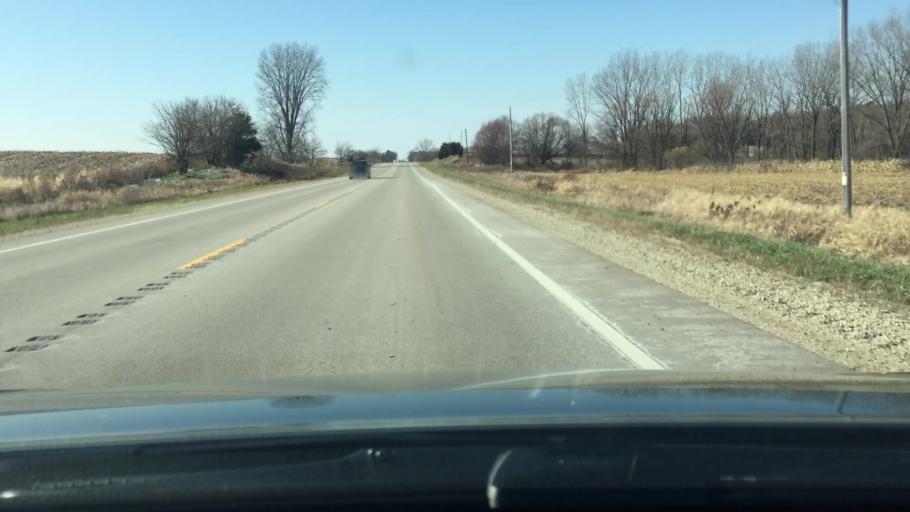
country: US
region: Wisconsin
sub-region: Jefferson County
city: Lake Mills
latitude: 43.0077
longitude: -88.9067
